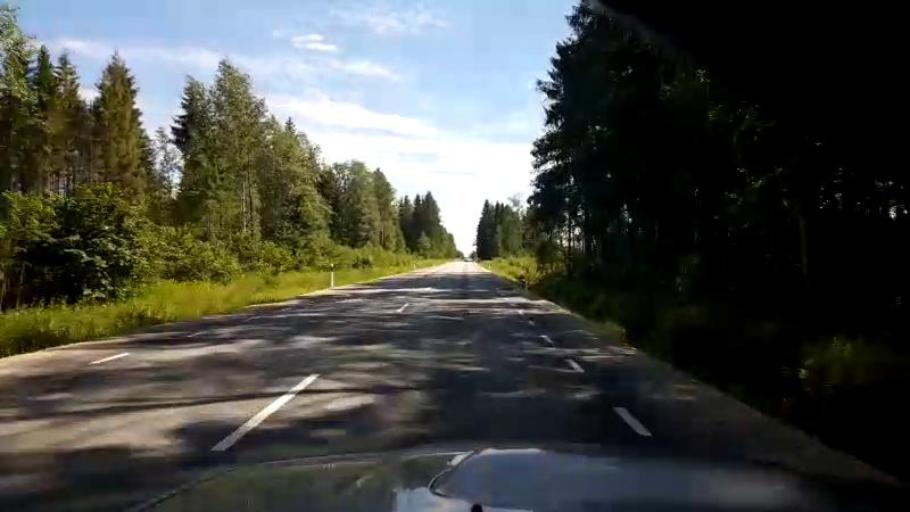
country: EE
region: Jogevamaa
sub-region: Jogeva linn
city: Jogeva
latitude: 58.7846
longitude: 26.3156
